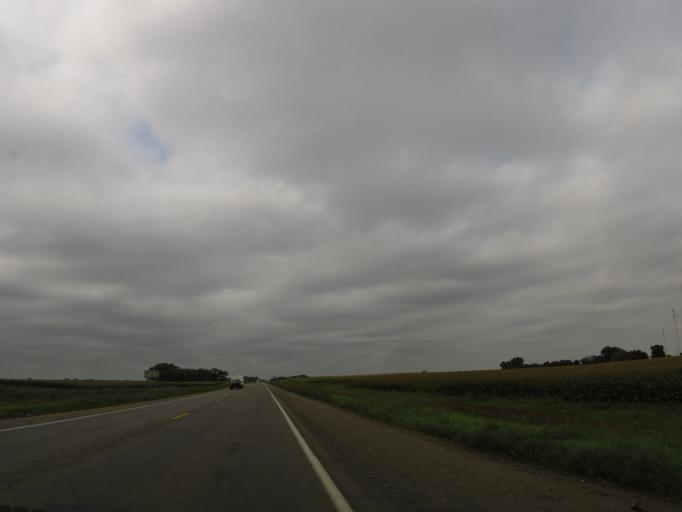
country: US
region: Minnesota
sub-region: Renville County
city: Renville
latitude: 44.7892
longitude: -95.2230
